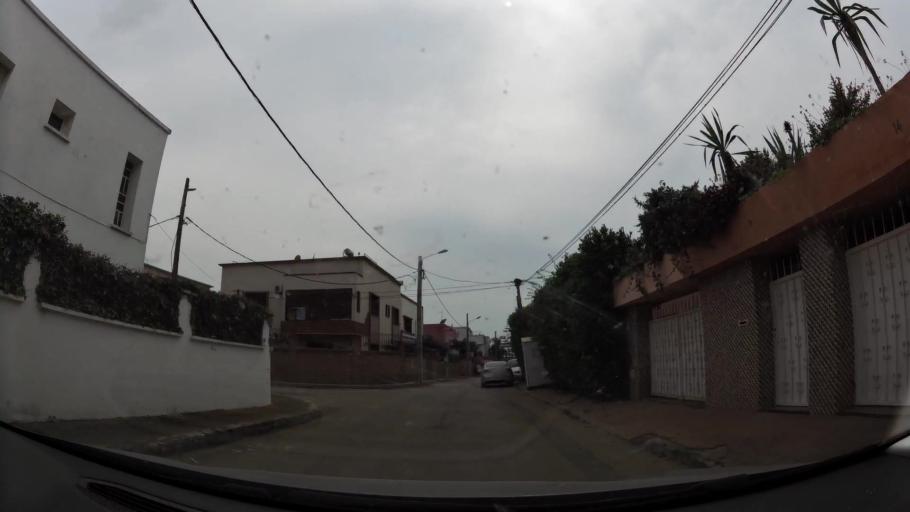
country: MA
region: Rabat-Sale-Zemmour-Zaer
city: Sale
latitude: 34.0323
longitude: -6.8124
